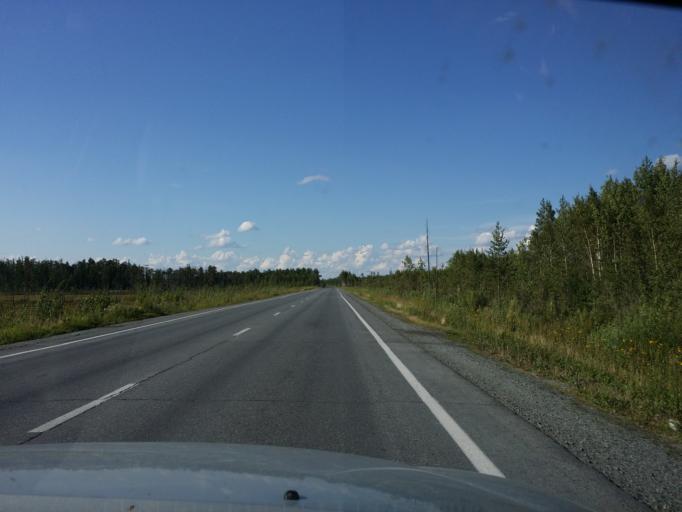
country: RU
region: Khanty-Mansiyskiy Avtonomnyy Okrug
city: Lokosovo
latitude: 61.3798
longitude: 74.9221
